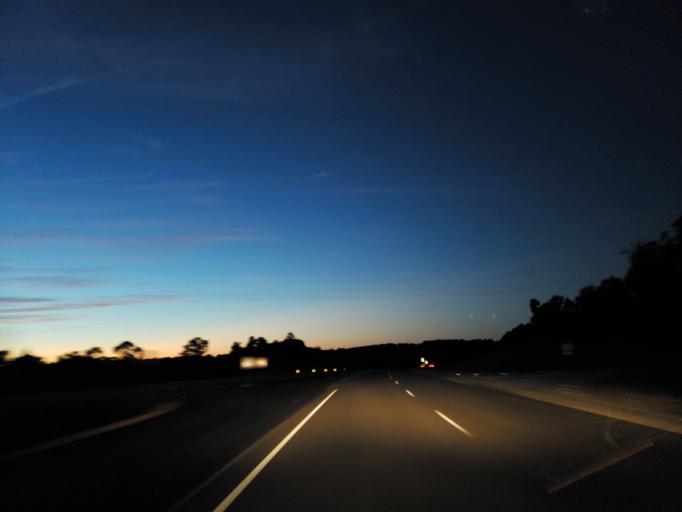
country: US
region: Mississippi
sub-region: Clarke County
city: Quitman
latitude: 32.1077
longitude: -88.7129
